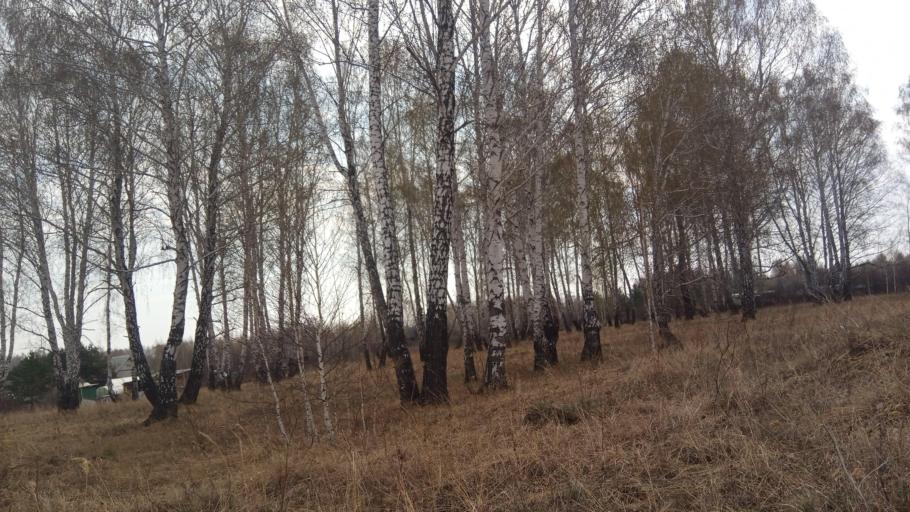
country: RU
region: Chelyabinsk
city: Timiryazevskiy
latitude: 54.9953
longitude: 60.8485
